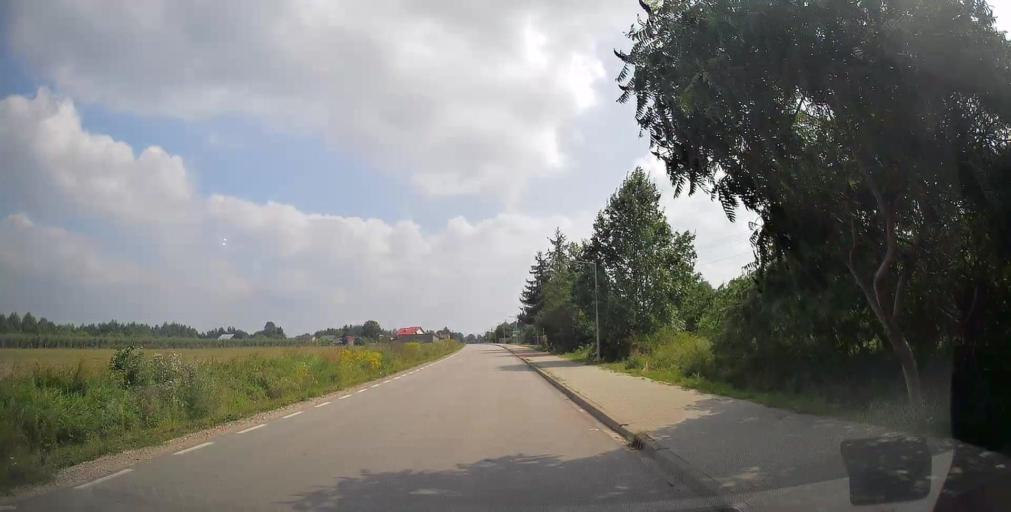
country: PL
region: Masovian Voivodeship
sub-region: Powiat bialobrzeski
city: Sucha
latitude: 51.6123
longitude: 20.9685
